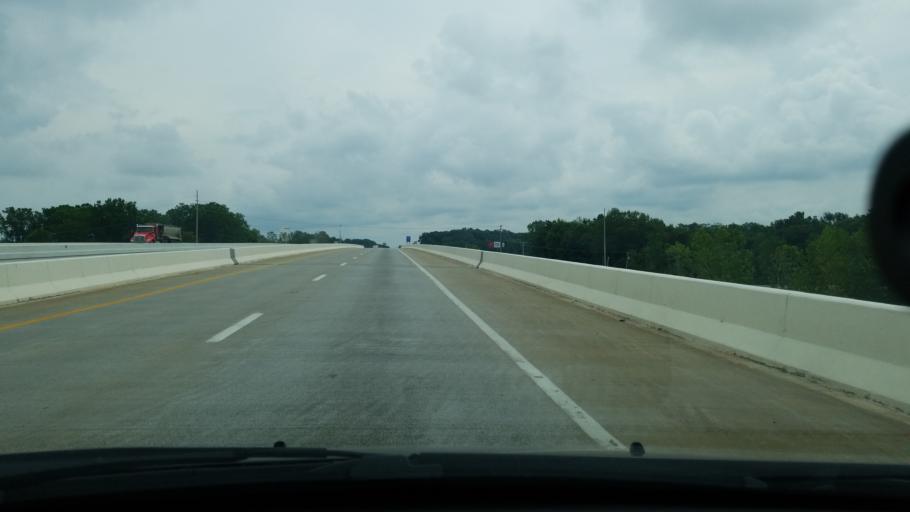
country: US
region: Ohio
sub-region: Erie County
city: Huron
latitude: 41.3697
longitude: -82.5474
